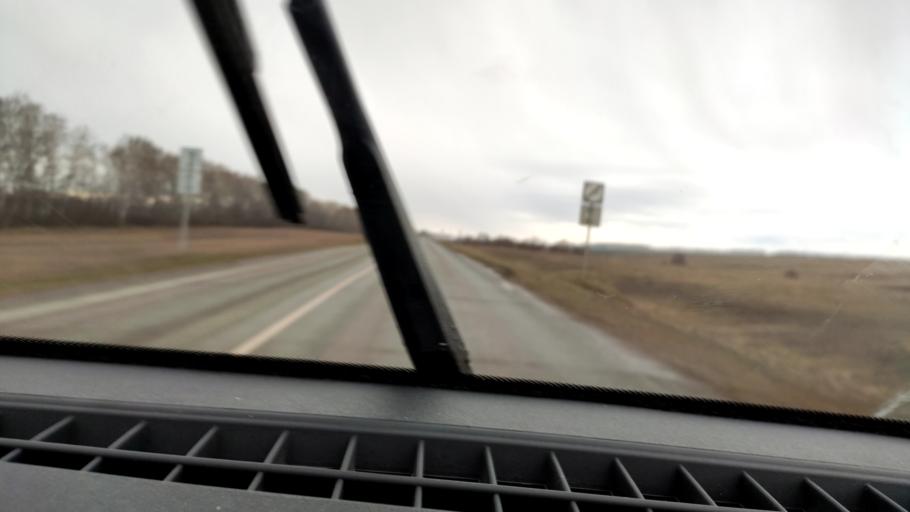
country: RU
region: Bashkortostan
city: Chekmagush
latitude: 55.1196
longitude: 54.7461
